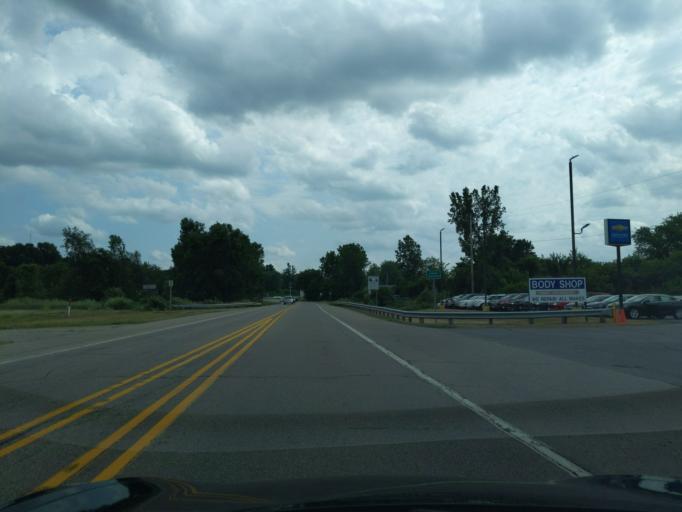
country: US
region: Michigan
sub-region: Eaton County
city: Eaton Rapids
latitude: 42.4934
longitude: -84.6586
